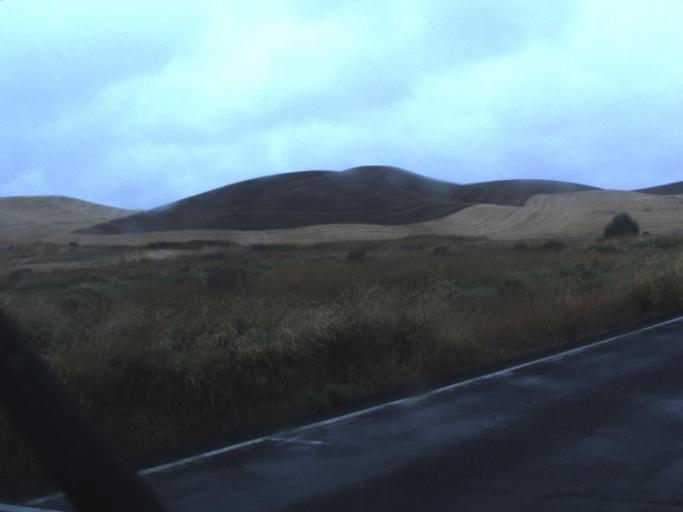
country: US
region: Washington
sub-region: Whitman County
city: Colfax
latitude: 47.0052
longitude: -117.3857
